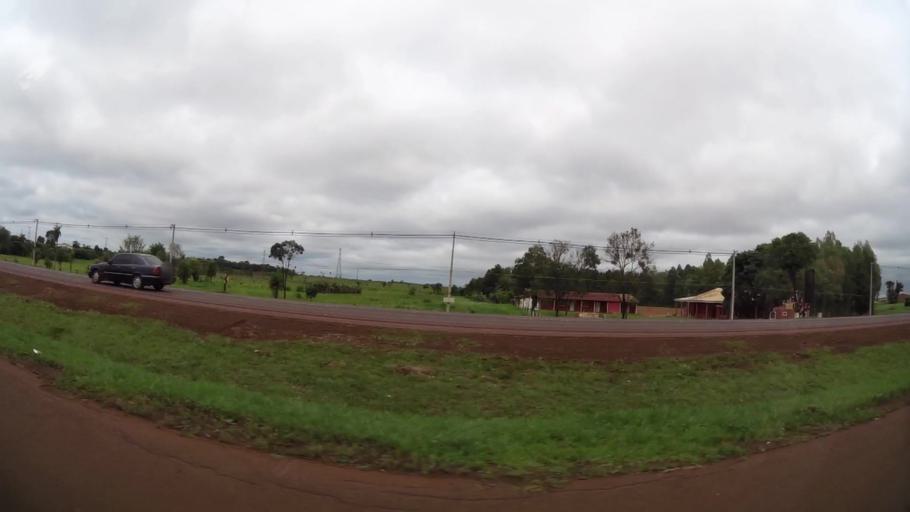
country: PY
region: Alto Parana
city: Presidente Franco
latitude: -25.4912
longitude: -54.7547
